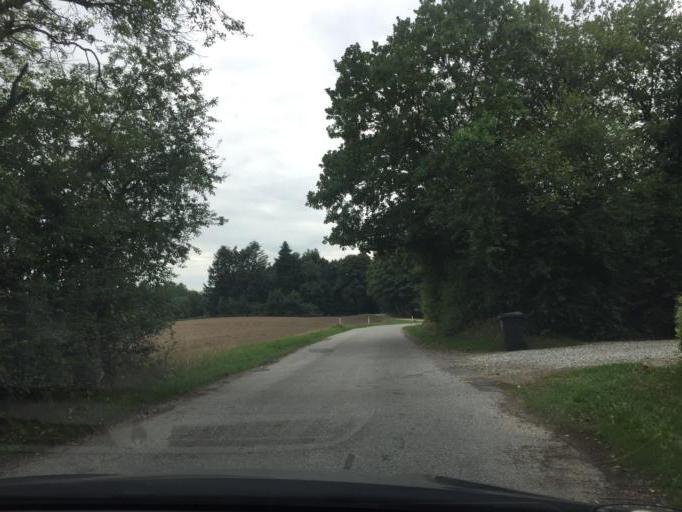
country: DK
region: South Denmark
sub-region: Assens Kommune
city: Arup
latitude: 55.3837
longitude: 10.0378
